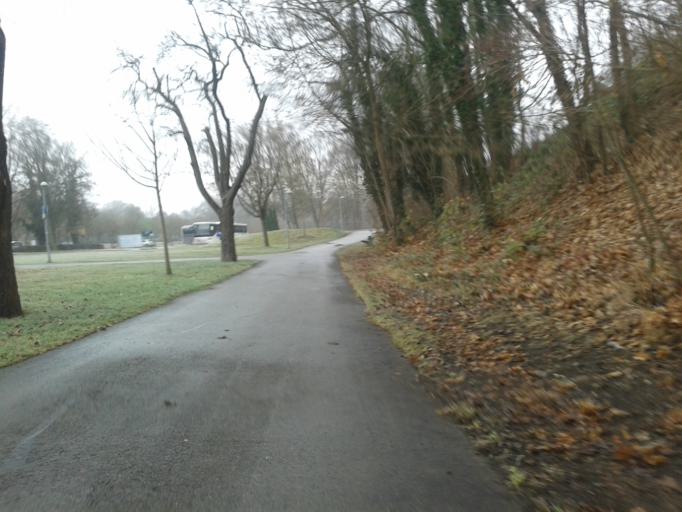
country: DE
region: Bavaria
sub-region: Swabia
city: Neu-Ulm
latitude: 48.4124
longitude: 10.0101
